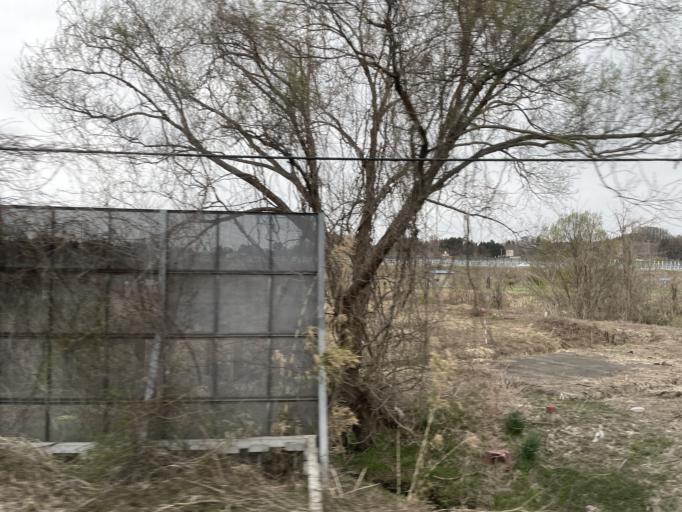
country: JP
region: Aomori
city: Namioka
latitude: 40.7125
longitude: 140.5824
